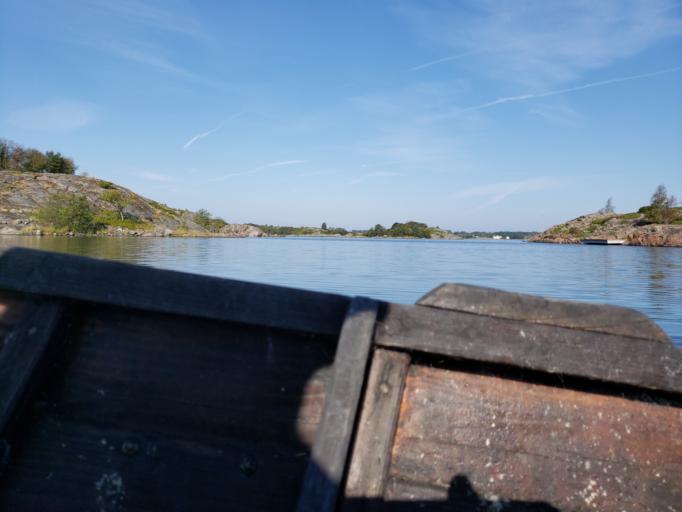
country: FI
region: Varsinais-Suomi
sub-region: Aboland-Turunmaa
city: Dragsfjaerd
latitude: 59.8597
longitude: 22.2081
